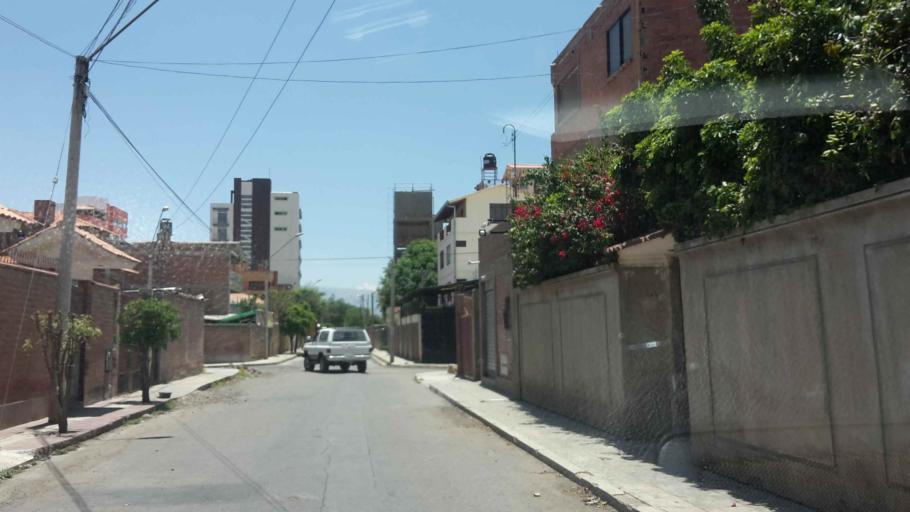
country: BO
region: Cochabamba
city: Cochabamba
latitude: -17.3852
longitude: -66.1864
